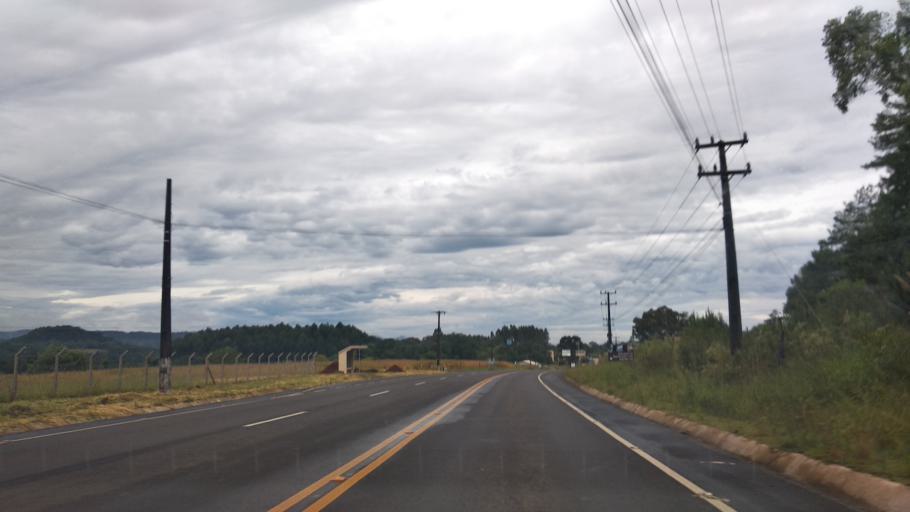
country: BR
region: Santa Catarina
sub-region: Videira
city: Videira
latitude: -27.0530
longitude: -51.1860
